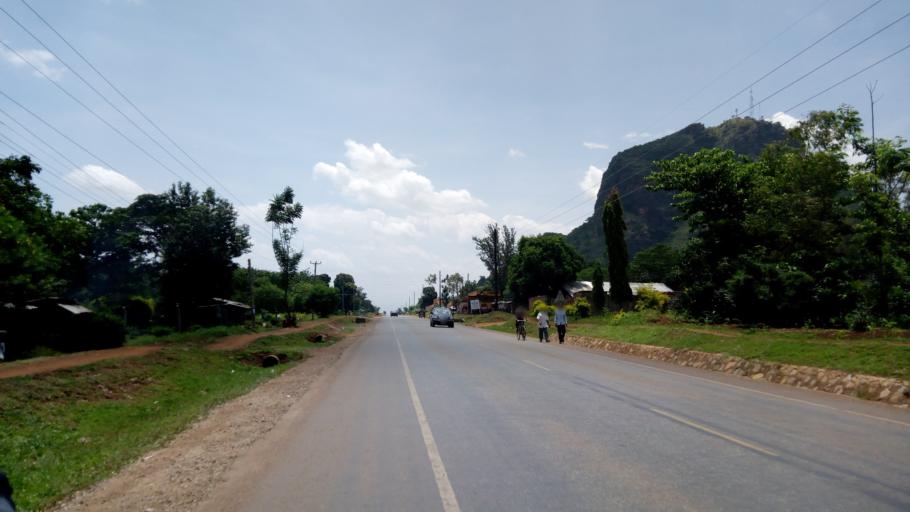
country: UG
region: Eastern Region
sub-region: Tororo District
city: Tororo
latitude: 0.6779
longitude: 34.1772
